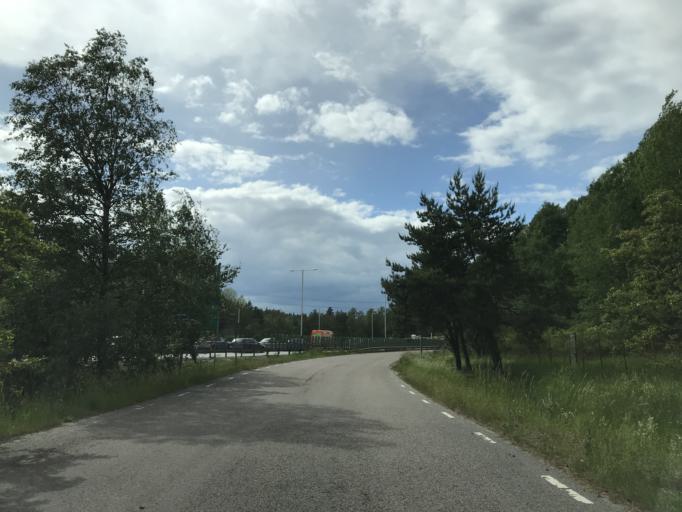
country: SE
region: Stockholm
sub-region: Solna Kommun
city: Rasunda
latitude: 59.3910
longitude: 17.9954
